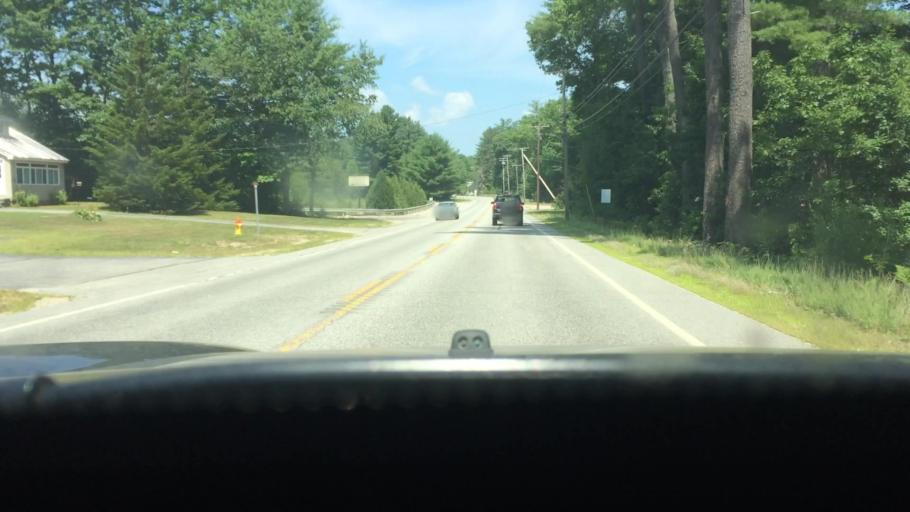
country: US
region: Maine
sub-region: Androscoggin County
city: Mechanic Falls
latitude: 44.1011
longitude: -70.3625
